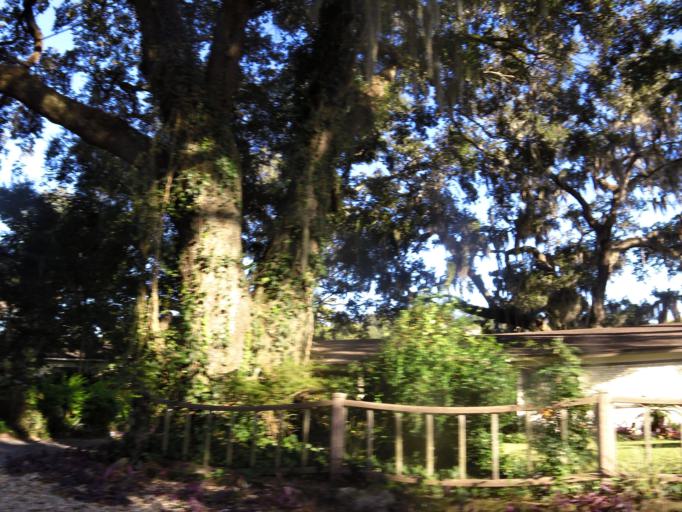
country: US
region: Florida
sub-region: Duval County
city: Jacksonville
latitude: 30.2637
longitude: -81.6435
